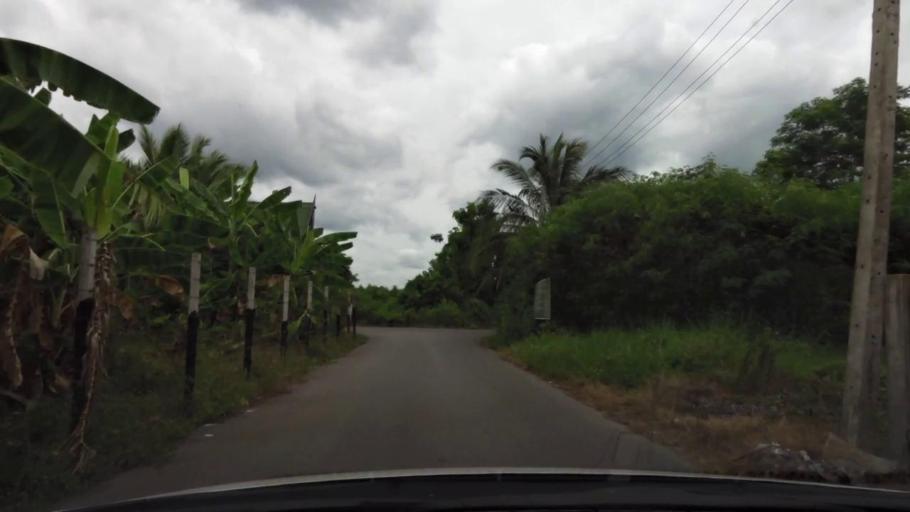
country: TH
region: Samut Sakhon
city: Ban Phaeo
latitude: 13.5670
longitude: 100.0329
